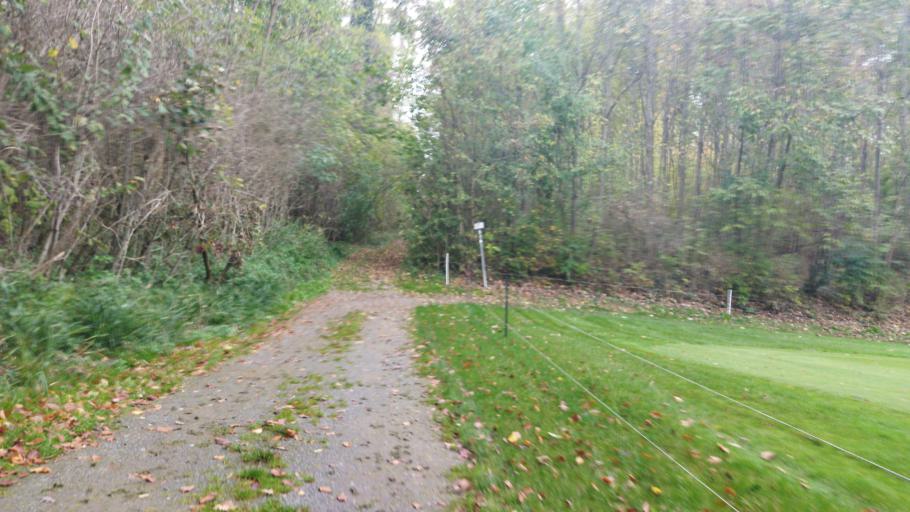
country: DE
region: Baden-Wuerttemberg
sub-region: Regierungsbezirk Stuttgart
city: Neckarwestheim
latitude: 49.0330
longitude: 9.1873
